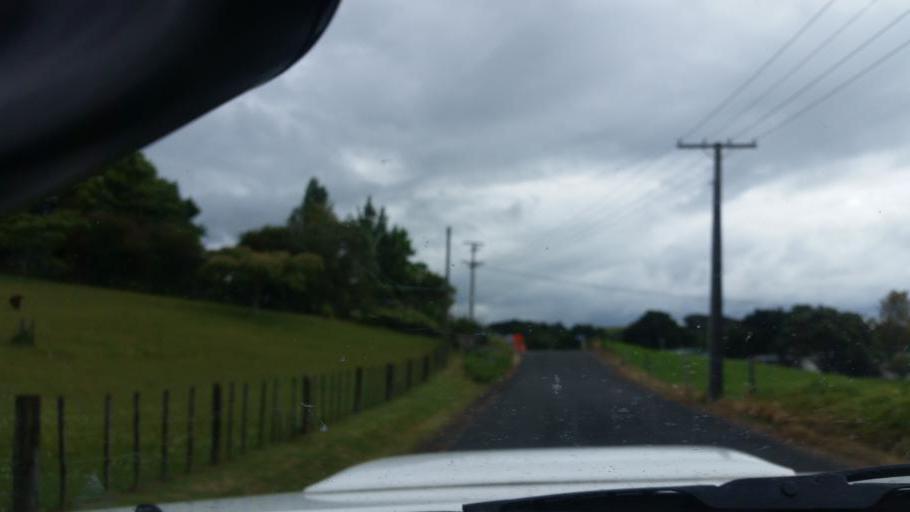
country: NZ
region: Auckland
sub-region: Auckland
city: Wellsford
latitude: -36.1552
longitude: 174.2234
